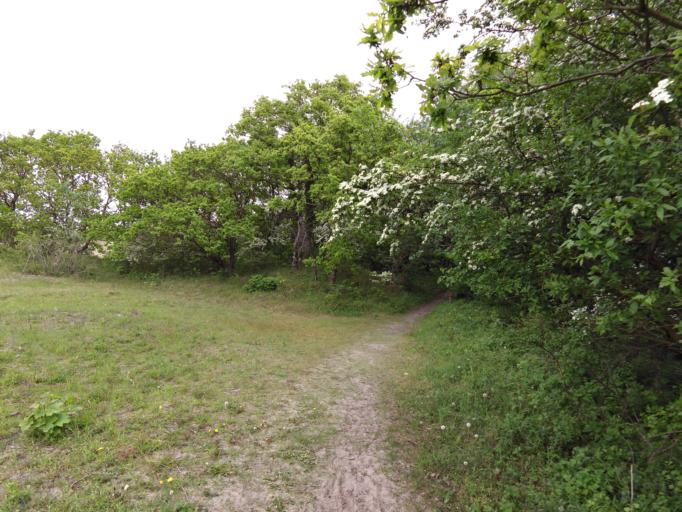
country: NL
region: South Holland
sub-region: Gemeente Rotterdam
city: Hoek van Holland
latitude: 51.9193
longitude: 4.0943
